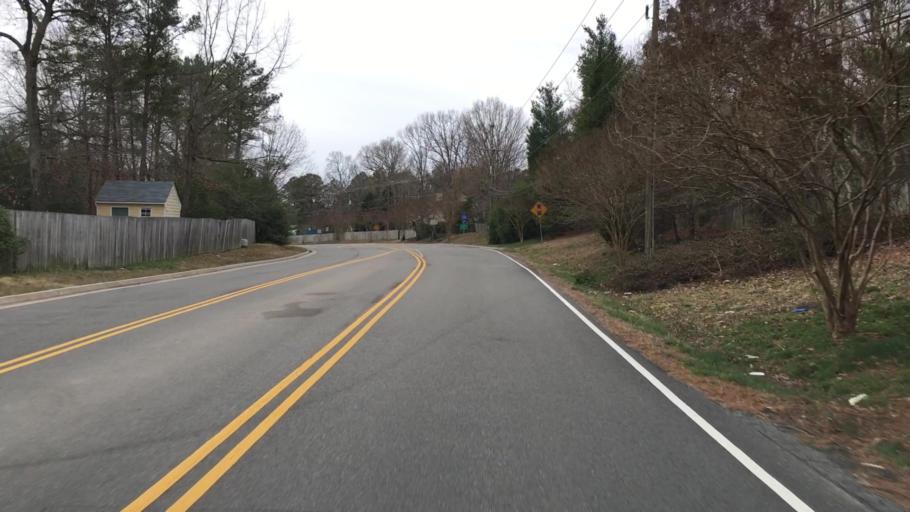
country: US
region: Virginia
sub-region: Henrico County
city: Short Pump
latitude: 37.6650
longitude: -77.5616
